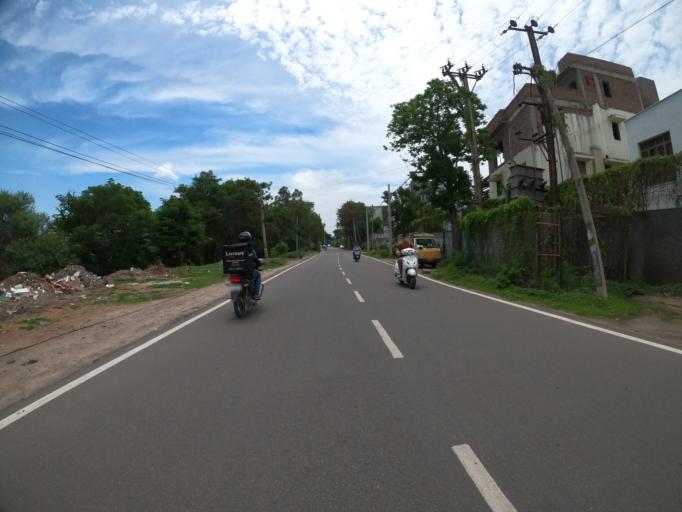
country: IN
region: Telangana
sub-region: Hyderabad
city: Hyderabad
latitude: 17.3712
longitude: 78.4248
